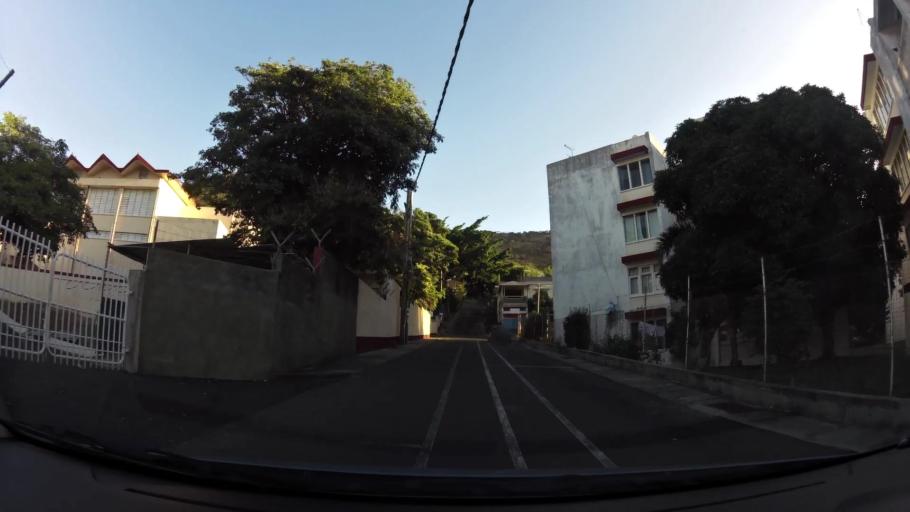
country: MU
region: Port Louis
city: Port Louis
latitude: -20.1749
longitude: 57.5052
